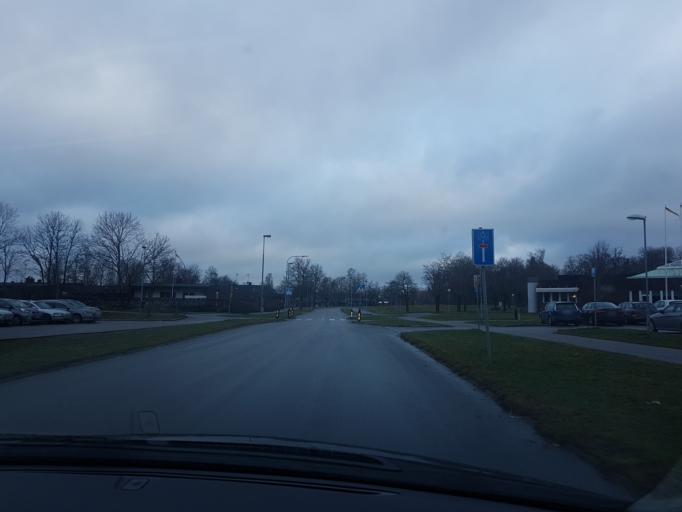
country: SE
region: Joenkoeping
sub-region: Vetlanda Kommun
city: Vetlanda
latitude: 57.4336
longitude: 15.0799
